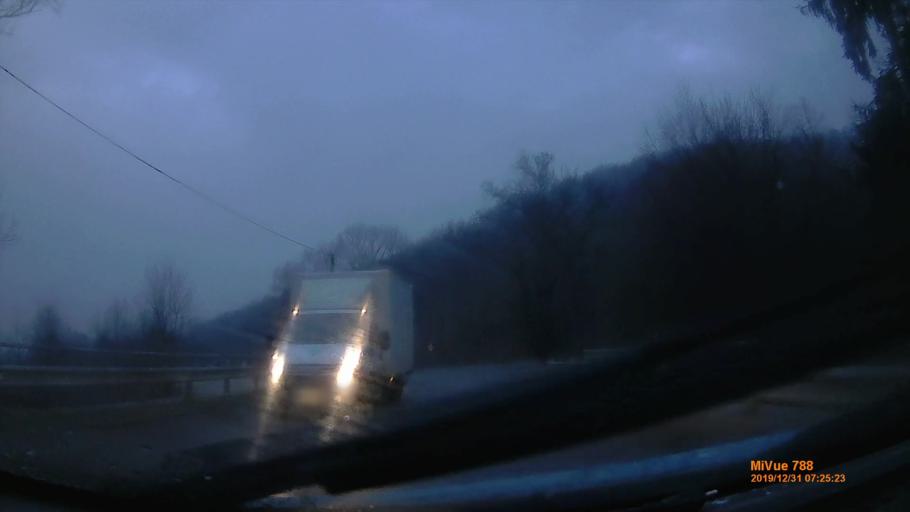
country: HU
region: Heves
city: Matraderecske
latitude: 47.9253
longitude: 20.0626
